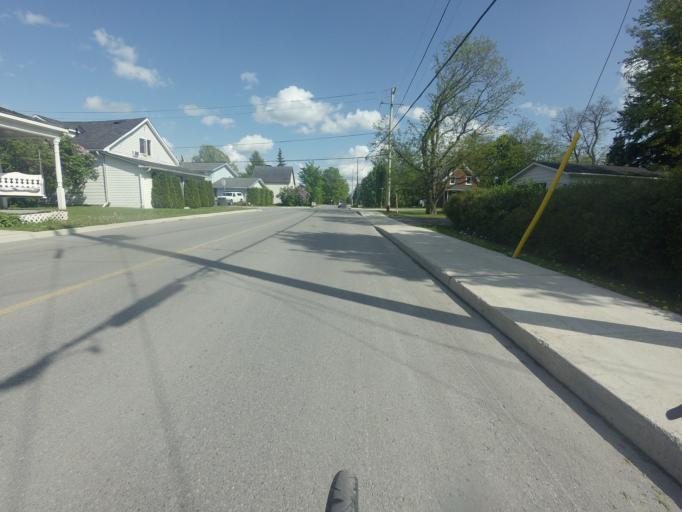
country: CA
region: Ontario
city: Carleton Place
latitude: 45.1379
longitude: -76.1334
